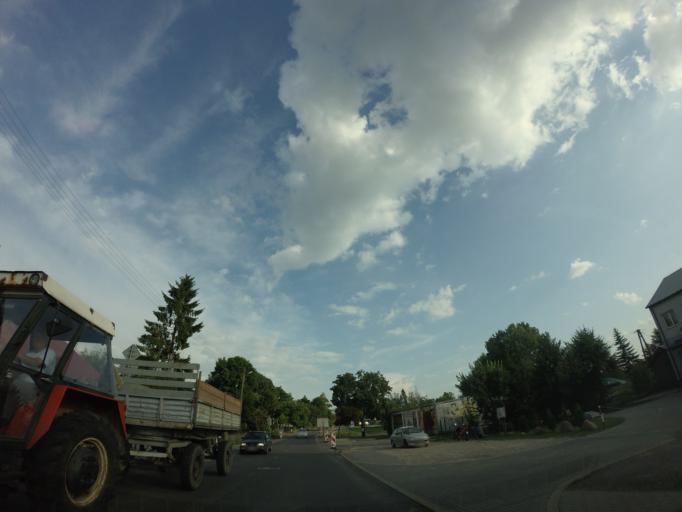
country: PL
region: Lublin Voivodeship
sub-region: Powiat lubartowski
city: Przytoczno
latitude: 51.6189
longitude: 22.2722
